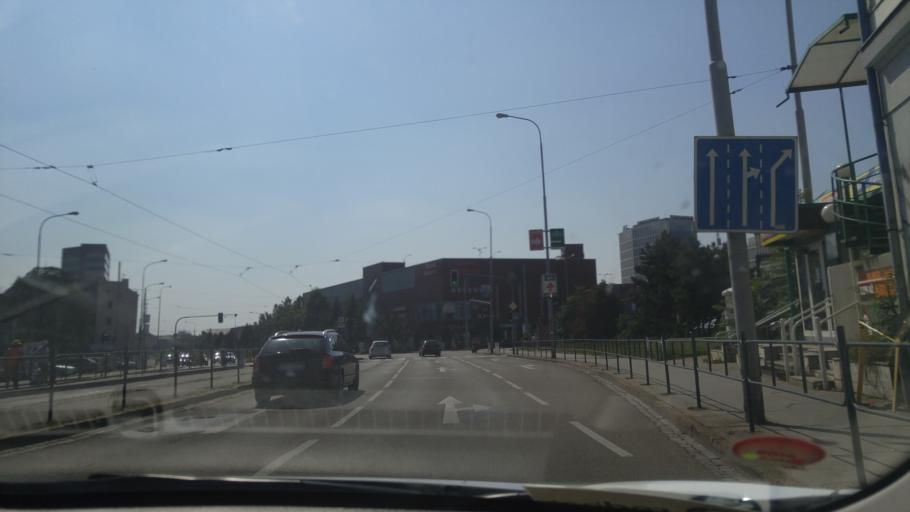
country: CZ
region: South Moravian
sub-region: Mesto Brno
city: Brno
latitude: 49.1903
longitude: 16.6144
